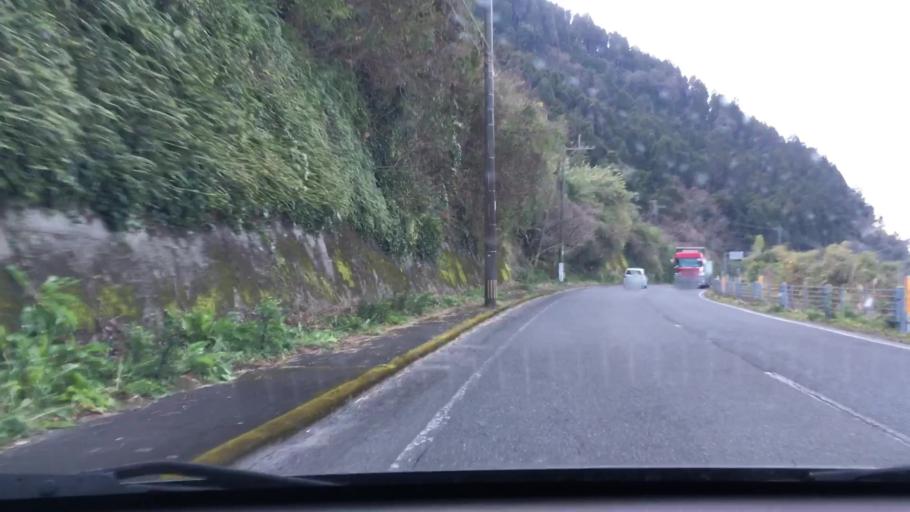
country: JP
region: Kagoshima
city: Kokubu-matsuki
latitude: 31.6350
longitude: 130.8049
